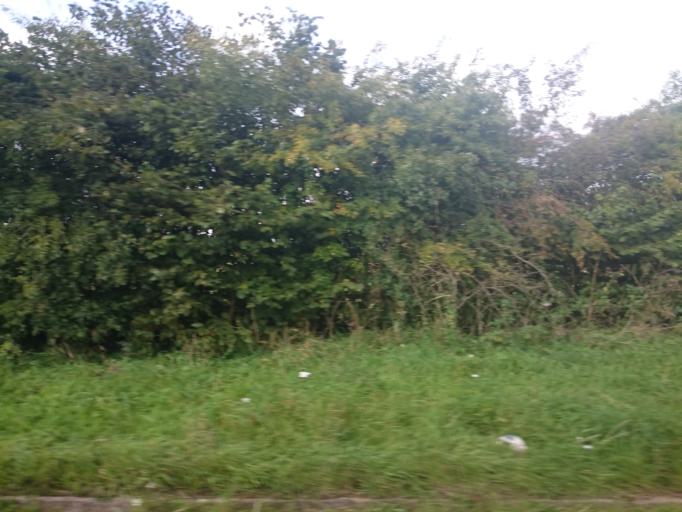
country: GB
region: England
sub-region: Gloucestershire
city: Charlton Kings
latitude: 51.7951
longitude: -2.0512
